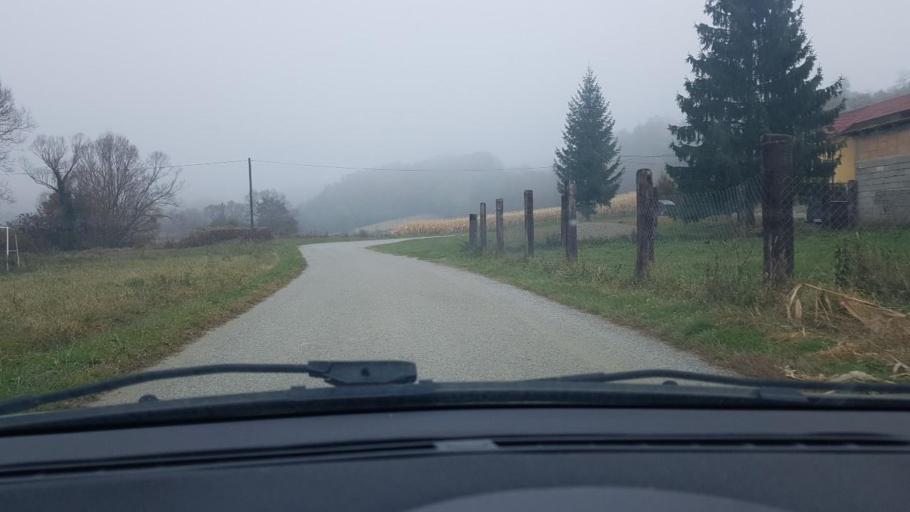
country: HR
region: Krapinsko-Zagorska
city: Mihovljan
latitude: 46.1496
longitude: 15.9868
